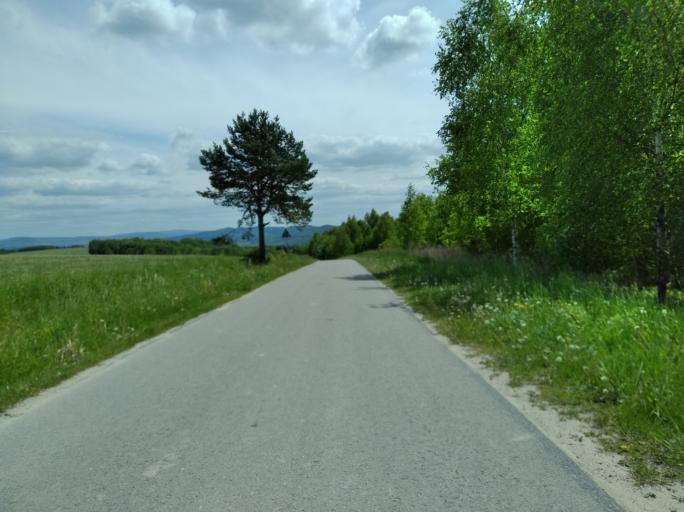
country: PL
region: Subcarpathian Voivodeship
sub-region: Powiat ropczycko-sedziszowski
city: Wielopole Skrzynskie
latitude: 49.8982
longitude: 21.6110
